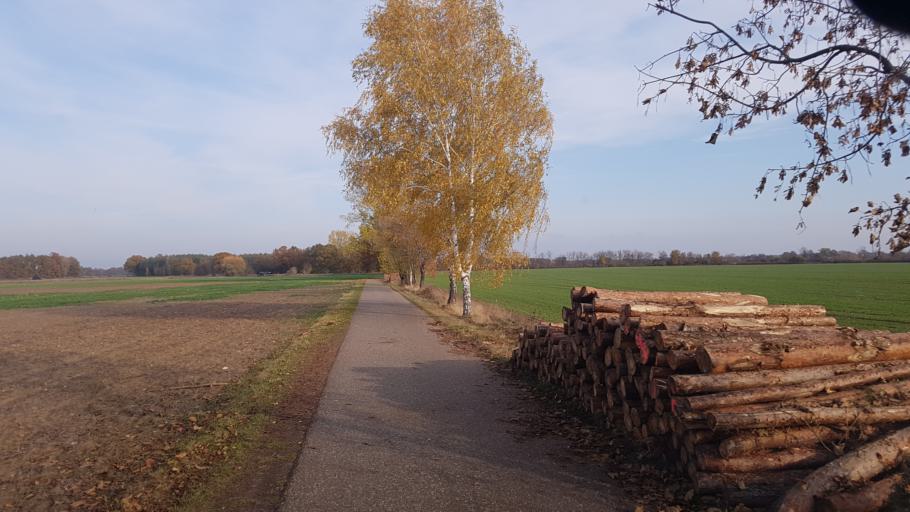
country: DE
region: Brandenburg
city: Falkenberg
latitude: 51.6006
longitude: 13.2819
